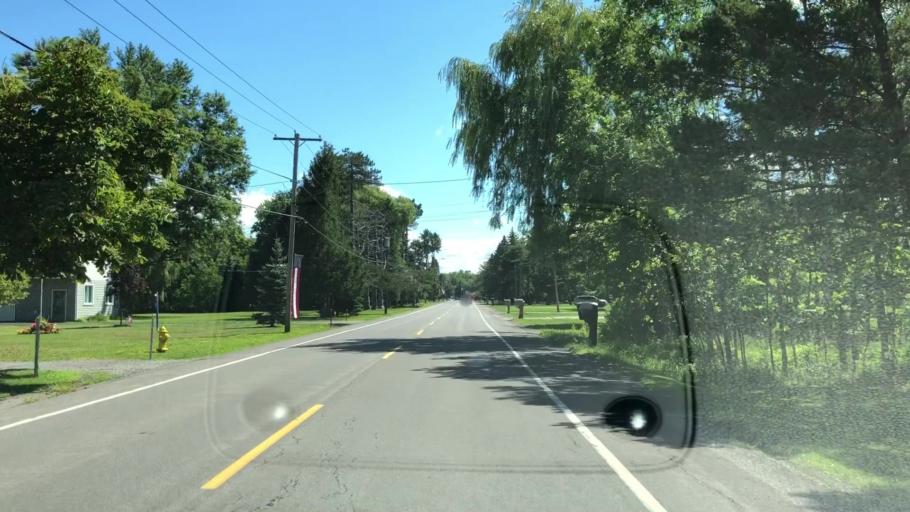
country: US
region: New York
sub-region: Erie County
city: Depew
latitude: 42.8508
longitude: -78.7171
